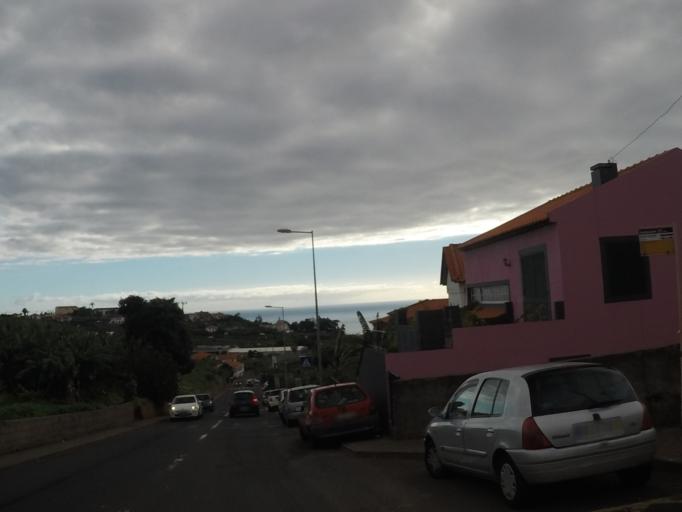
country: PT
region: Madeira
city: Camara de Lobos
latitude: 32.6538
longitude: -16.9560
